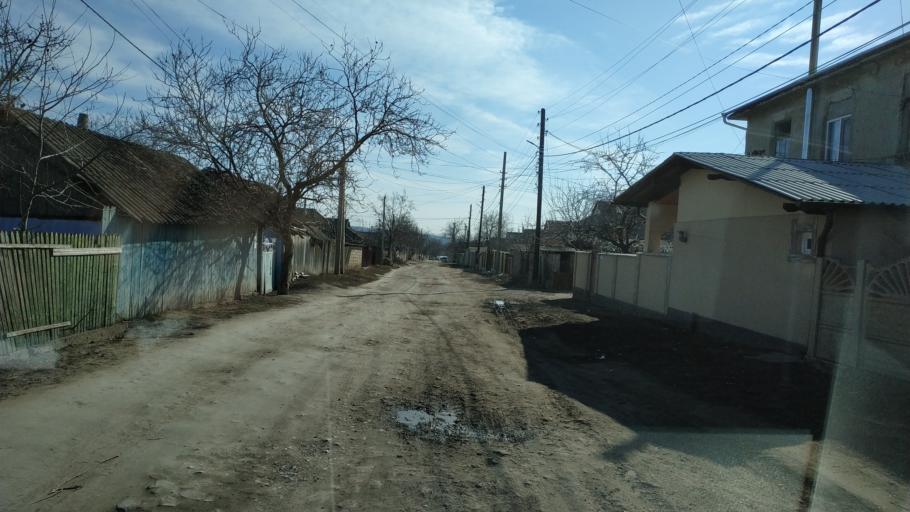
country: MD
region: Nisporeni
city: Nisporeni
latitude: 47.0794
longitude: 28.1620
